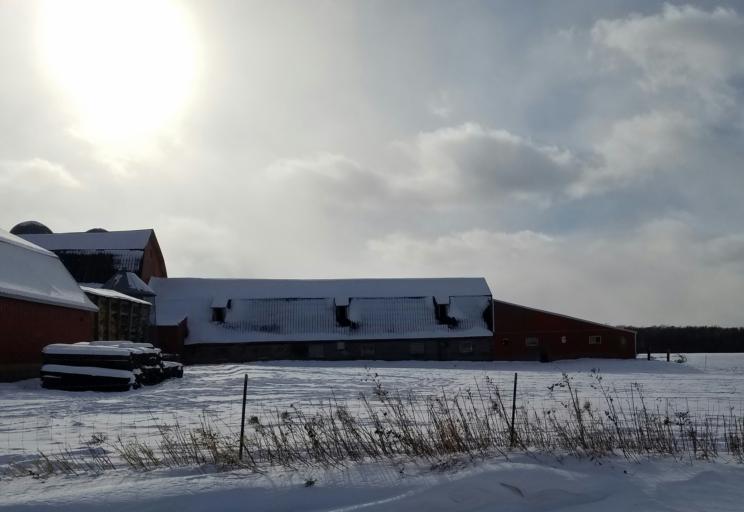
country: US
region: Wisconsin
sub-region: Clark County
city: Loyal
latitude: 44.6399
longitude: -90.4252
